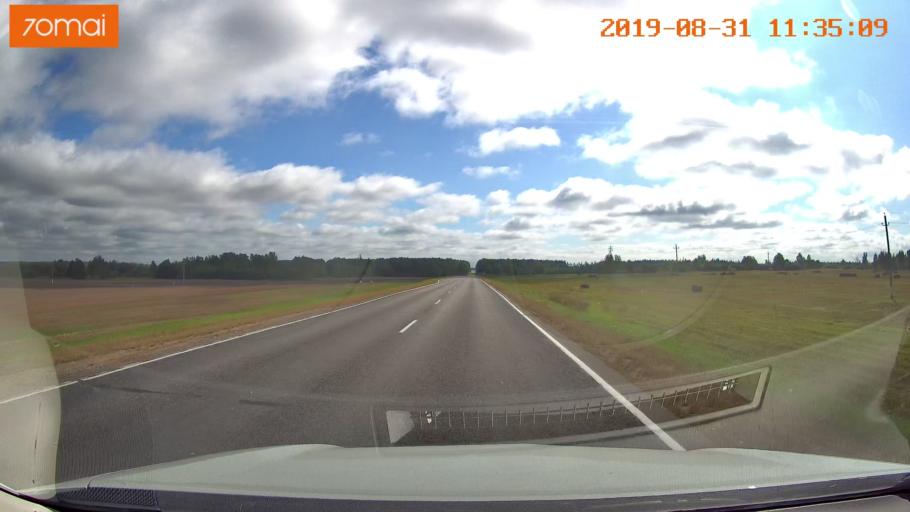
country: BY
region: Mogilev
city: Cherykaw
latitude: 53.6706
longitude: 31.2130
